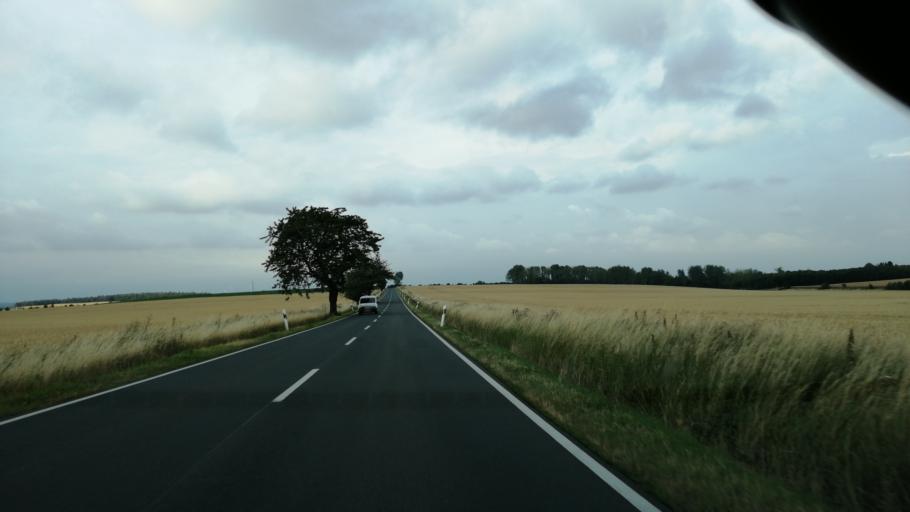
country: DE
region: Saxony-Anhalt
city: Mansfeld
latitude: 51.5721
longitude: 11.4480
